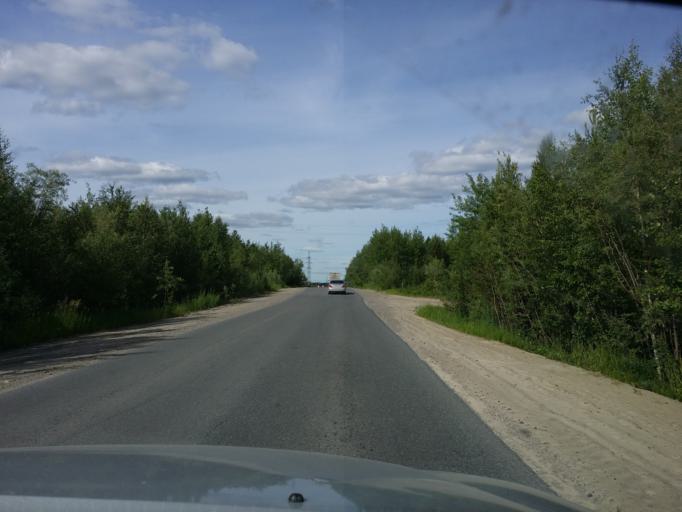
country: RU
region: Khanty-Mansiyskiy Avtonomnyy Okrug
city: Nizhnevartovsk
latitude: 60.9949
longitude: 76.5634
